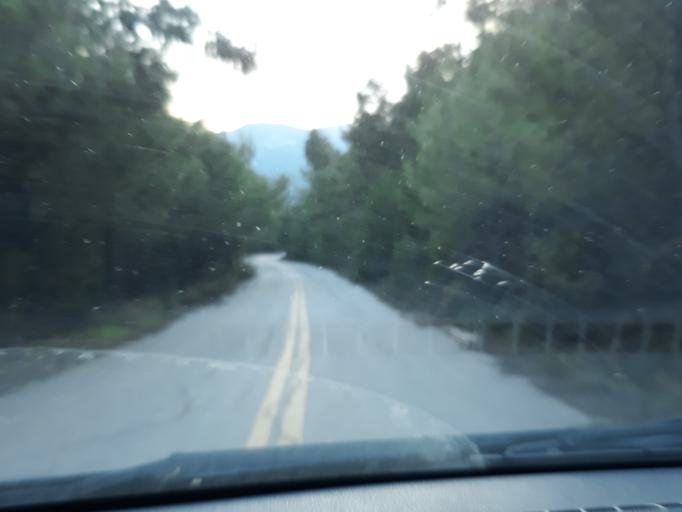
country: GR
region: Attica
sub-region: Nomarchia Anatolikis Attikis
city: Afidnes
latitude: 38.2117
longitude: 23.8146
